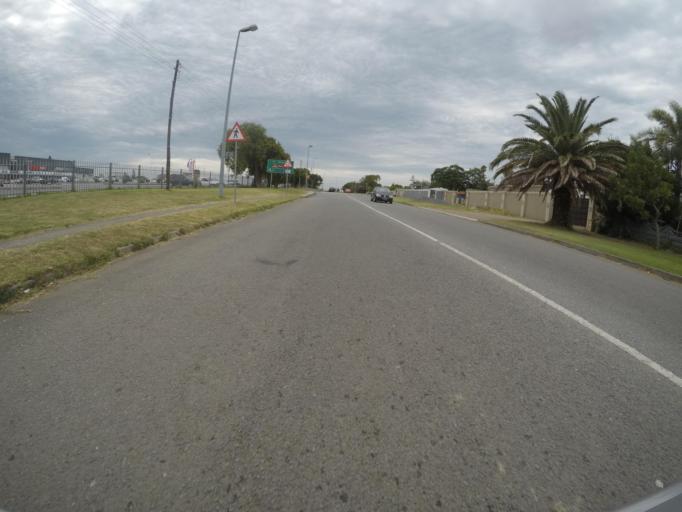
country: ZA
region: Eastern Cape
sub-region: Buffalo City Metropolitan Municipality
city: East London
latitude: -32.9683
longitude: 27.9414
